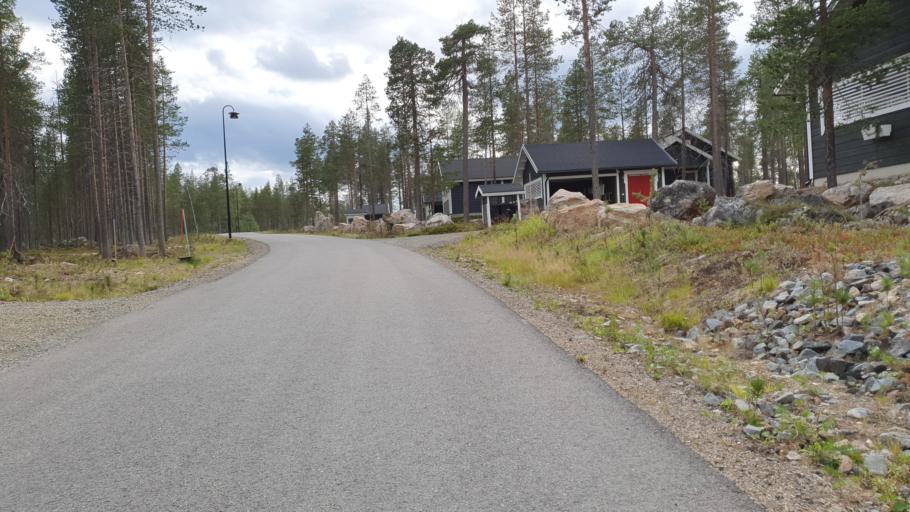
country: FI
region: Lapland
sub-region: Tunturi-Lappi
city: Kolari
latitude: 67.5900
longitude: 24.1232
